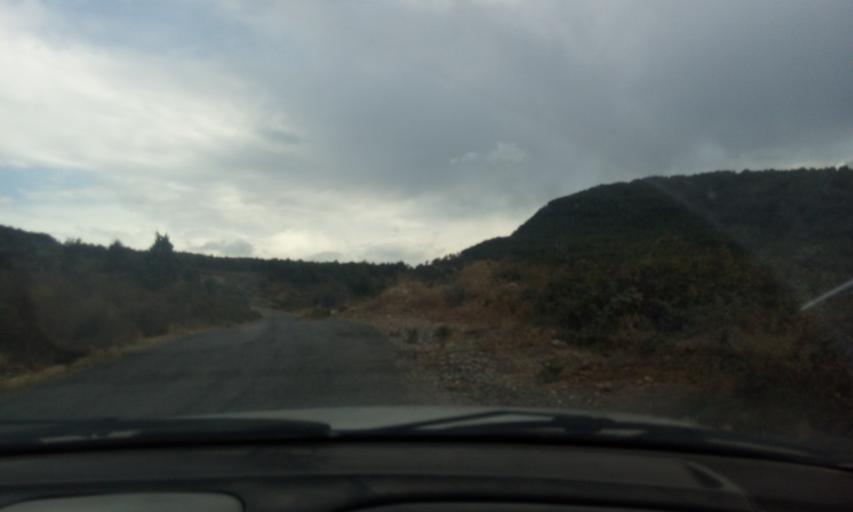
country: DZ
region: Tizi Ouzou
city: Chemini
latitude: 36.6183
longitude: 4.5061
